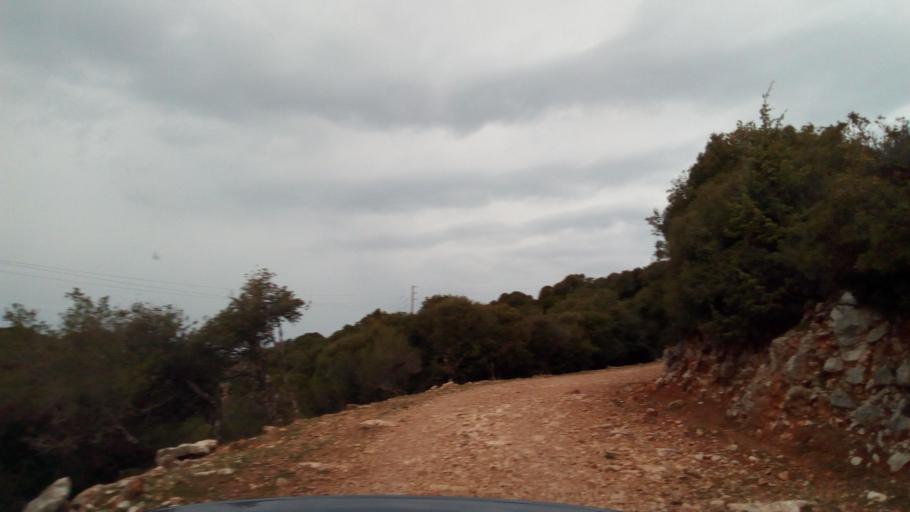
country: GR
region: West Greece
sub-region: Nomos Achaias
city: Kamarai
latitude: 38.4138
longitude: 22.0402
